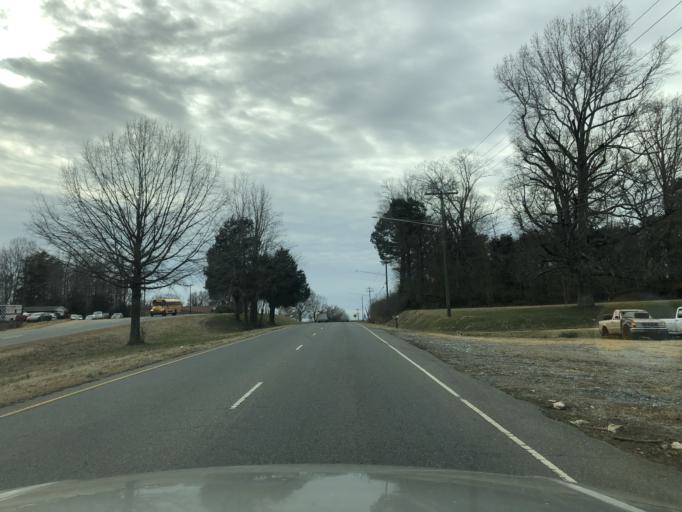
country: US
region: North Carolina
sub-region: Gaston County
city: South Gastonia
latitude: 35.2577
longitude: -81.2364
